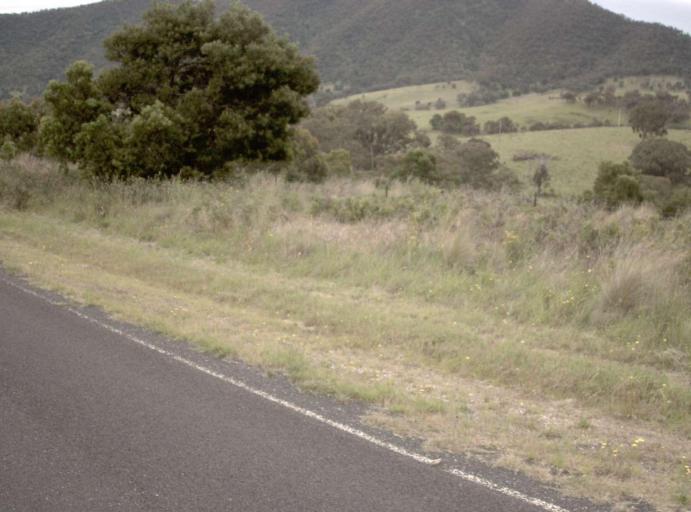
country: AU
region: Victoria
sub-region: East Gippsland
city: Bairnsdale
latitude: -37.5643
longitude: 147.1900
